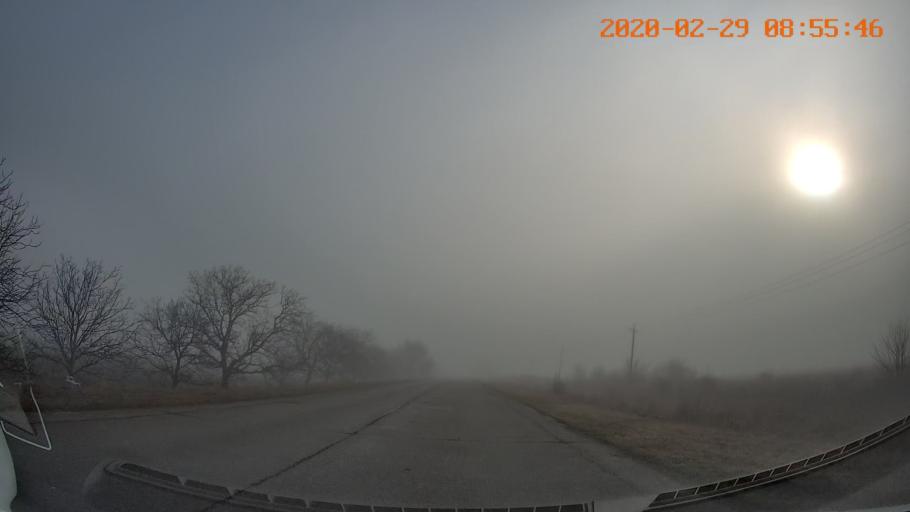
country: MD
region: Telenesti
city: Tiraspolul Nou
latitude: 46.9288
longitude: 29.5978
